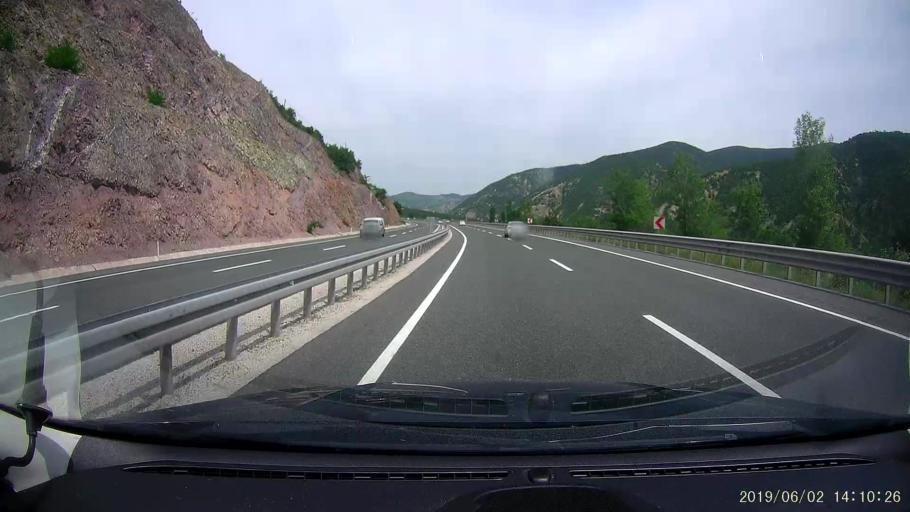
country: TR
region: Cankiri
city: Ilgaz
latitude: 40.9030
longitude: 33.7610
